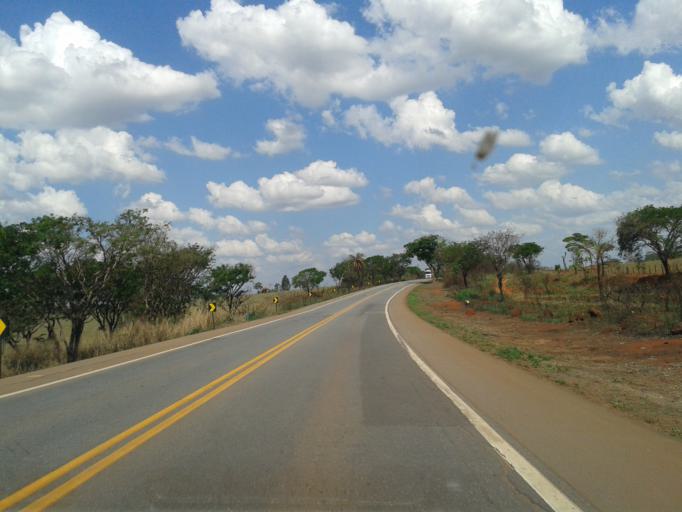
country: BR
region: Minas Gerais
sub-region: Luz
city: Luz
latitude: -19.7655
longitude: -45.7887
